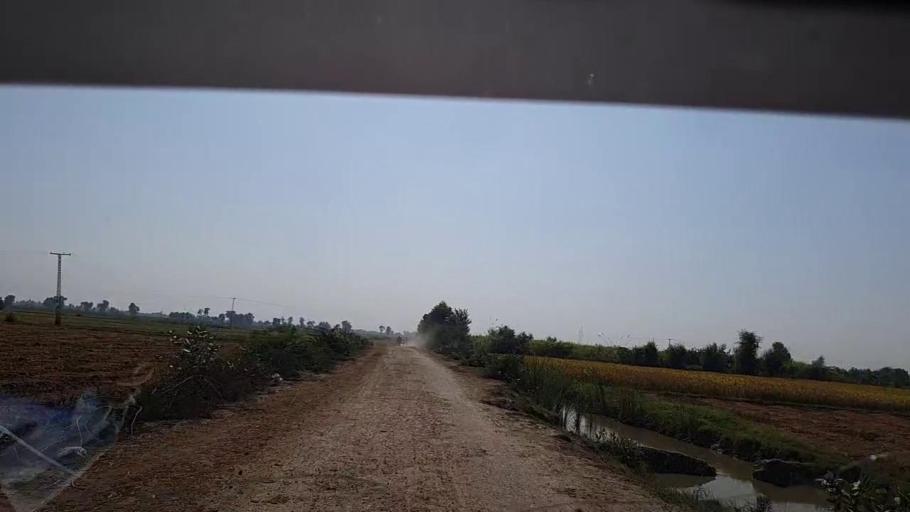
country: PK
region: Sindh
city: Naudero
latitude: 27.6949
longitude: 68.4022
